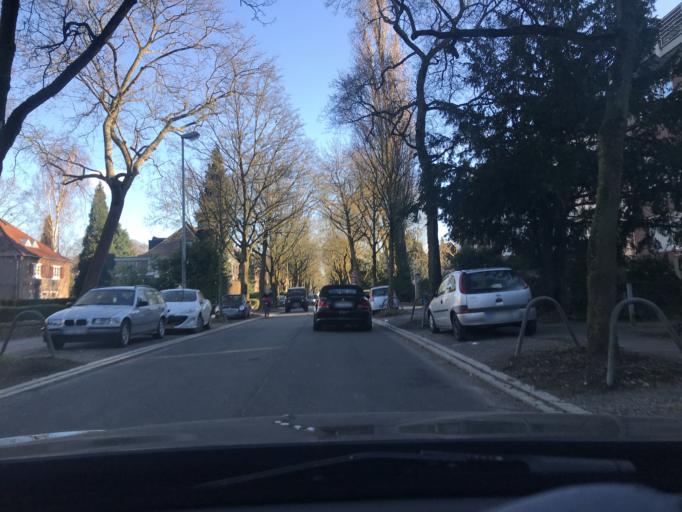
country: DE
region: North Rhine-Westphalia
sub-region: Regierungsbezirk Dusseldorf
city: Krefeld
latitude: 51.3388
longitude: 6.5924
